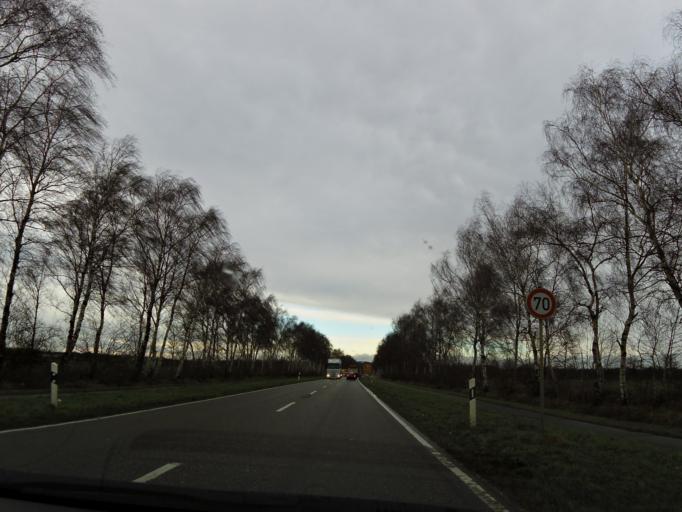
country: DE
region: North Rhine-Westphalia
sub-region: Regierungsbezirk Koln
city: Selfkant
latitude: 51.0175
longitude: 5.9455
